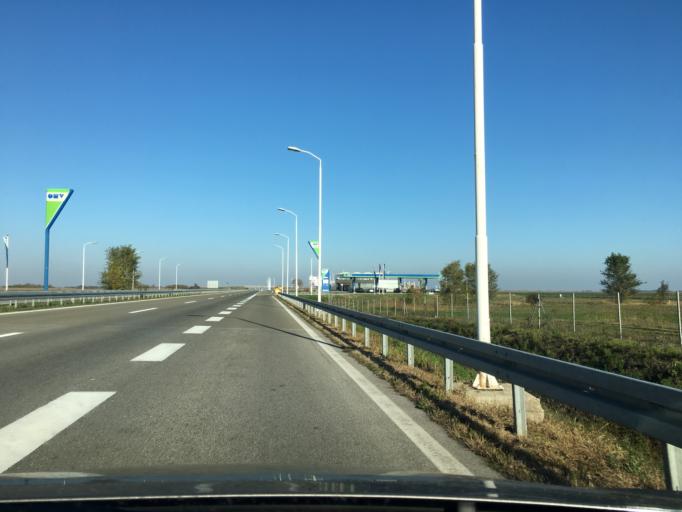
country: RS
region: Autonomna Pokrajina Vojvodina
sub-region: Severnobacki Okrug
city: Backa Topola
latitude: 45.7928
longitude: 19.6943
